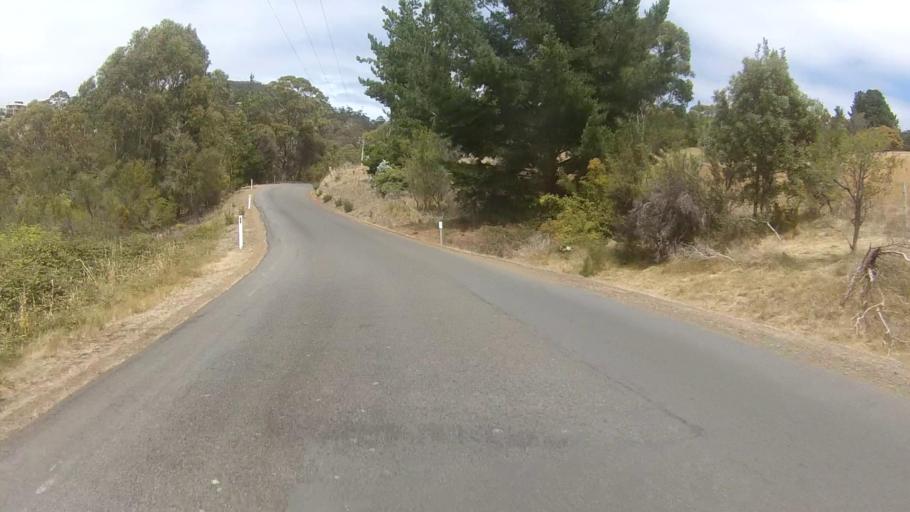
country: AU
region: Tasmania
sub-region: Kingborough
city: Blackmans Bay
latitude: -43.0420
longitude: 147.3360
